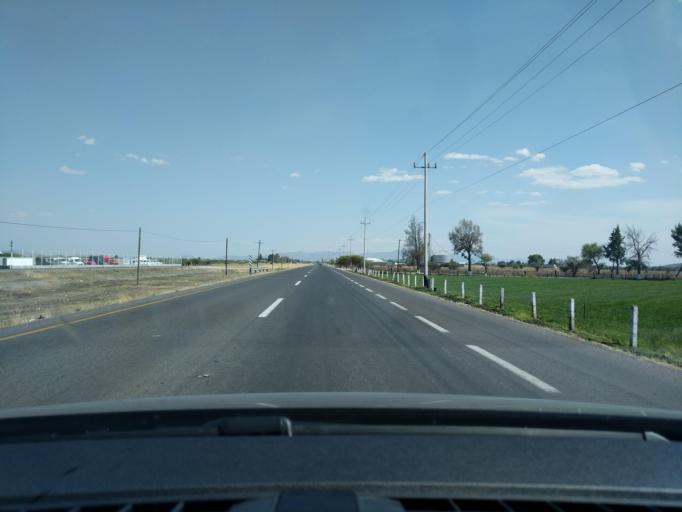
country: MX
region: Durango
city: Victoria de Durango
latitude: 24.0881
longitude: -104.5659
